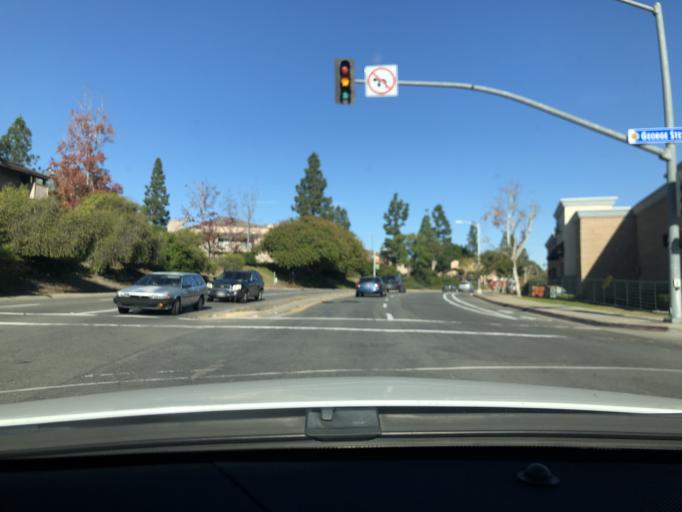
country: US
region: California
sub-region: San Diego County
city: Lemon Grove
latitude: 32.7418
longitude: -117.0565
